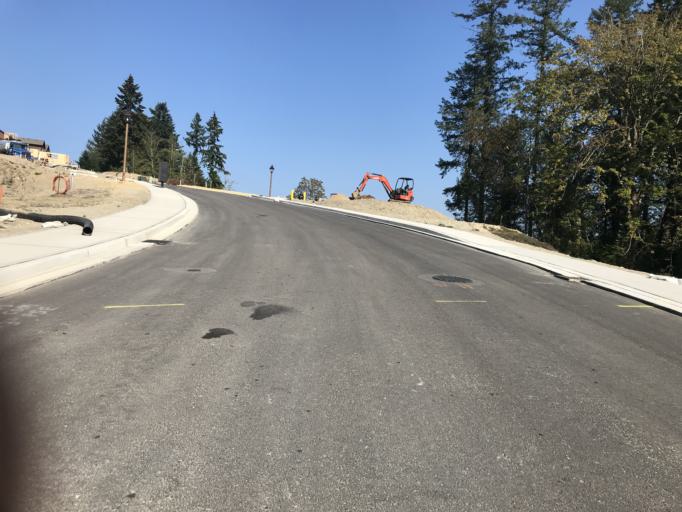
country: US
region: Washington
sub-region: Kitsap County
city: Poulsbo
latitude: 47.7249
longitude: -122.6245
